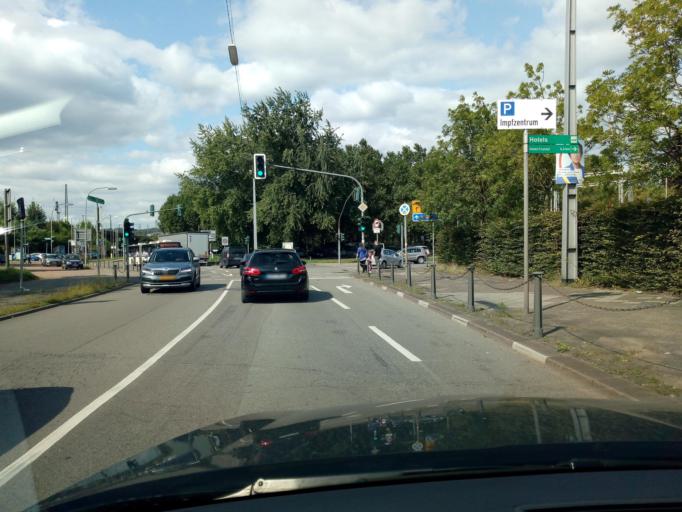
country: DE
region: Saarland
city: Saarbrucken
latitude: 49.2317
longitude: 6.9627
